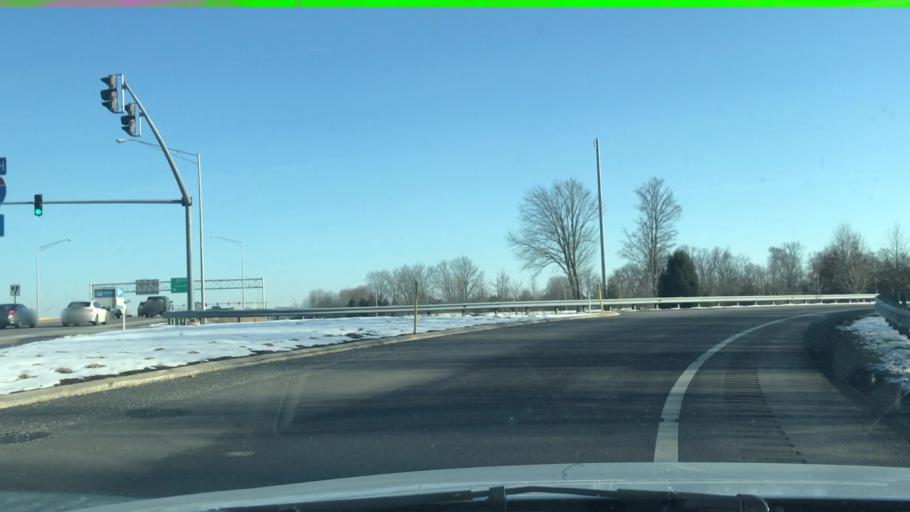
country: US
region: Kentucky
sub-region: Warren County
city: Bowling Green
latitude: 36.9783
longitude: -86.3924
